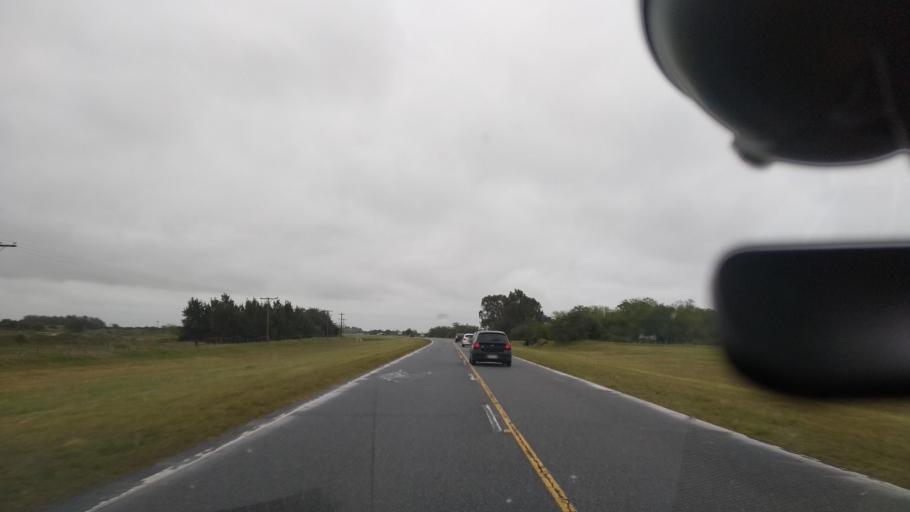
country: AR
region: Buenos Aires
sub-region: Partido de Castelli
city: Castelli
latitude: -35.9660
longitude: -57.4488
